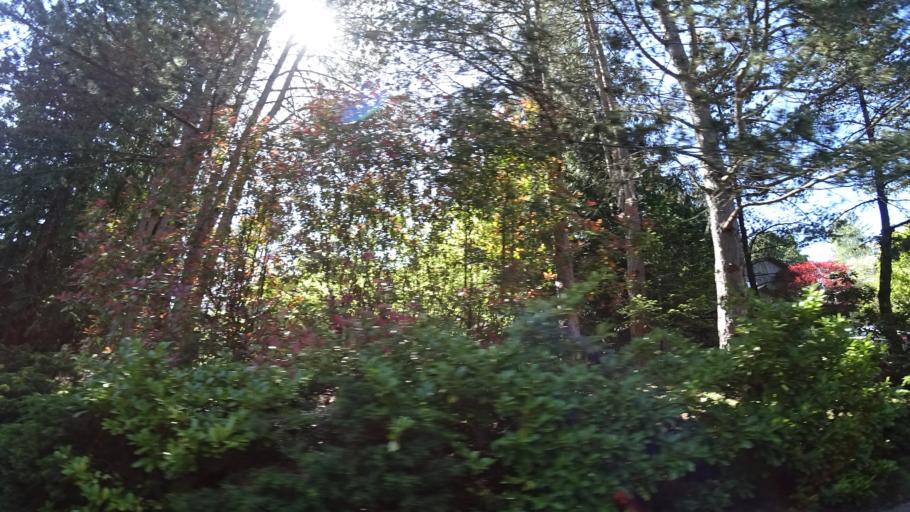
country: US
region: Oregon
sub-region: Washington County
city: Raleigh Hills
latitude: 45.4935
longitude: -122.7340
